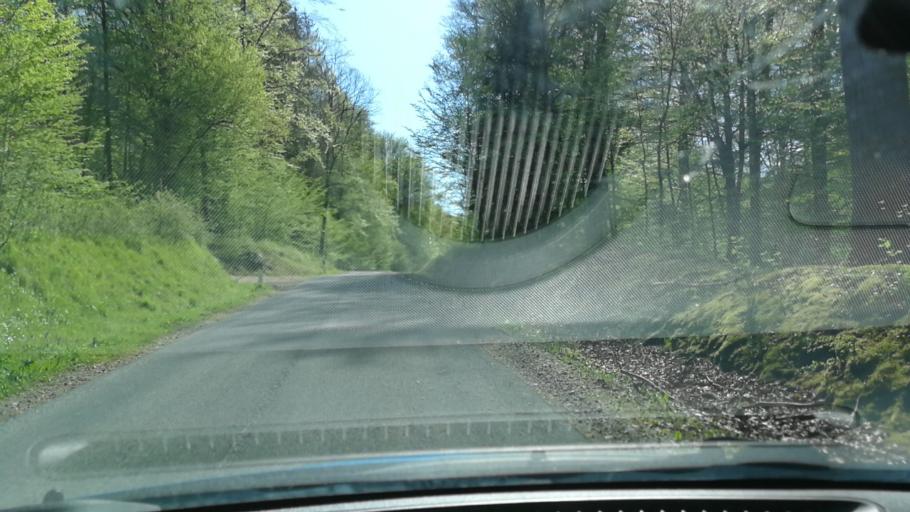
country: DE
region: Lower Saxony
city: Buhren
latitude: 51.5406
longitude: 9.6583
